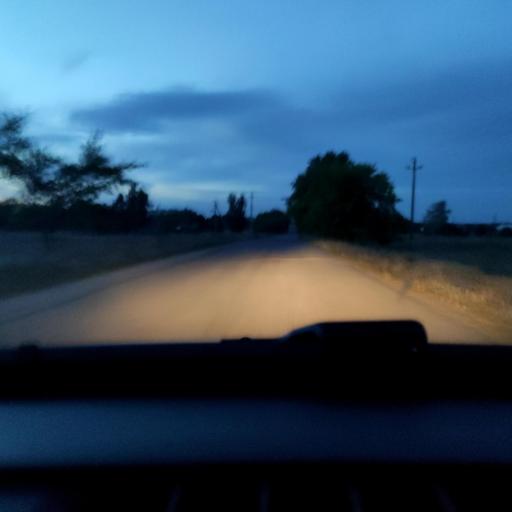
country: RU
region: Voronezj
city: Sadovoye
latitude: 51.6239
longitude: 40.4893
